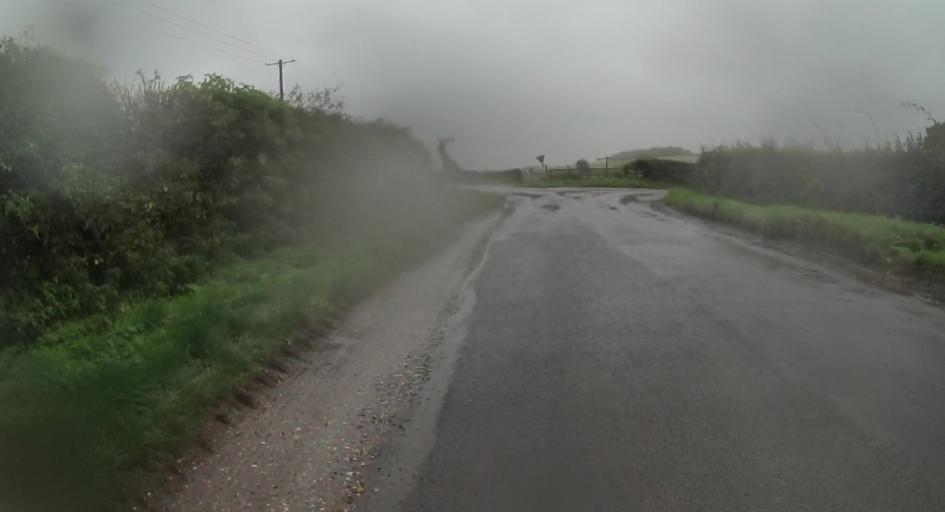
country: GB
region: England
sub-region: Hampshire
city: Four Marks
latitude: 51.1579
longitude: -1.1175
